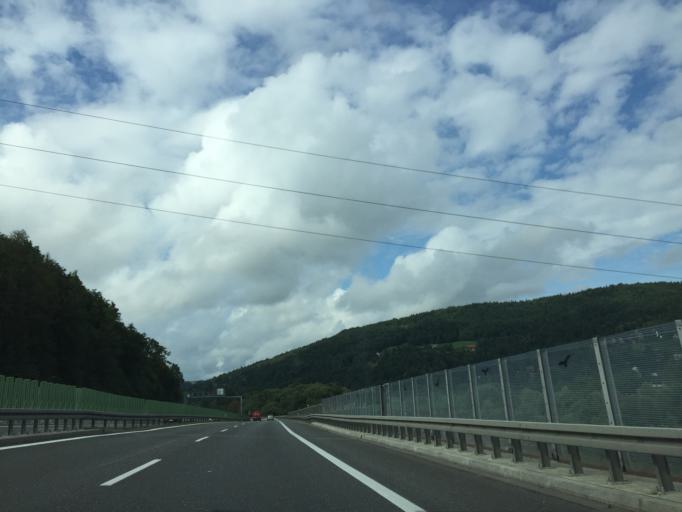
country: PL
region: Lesser Poland Voivodeship
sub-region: Powiat myslenicki
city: Stroza
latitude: 49.7961
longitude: 19.9236
